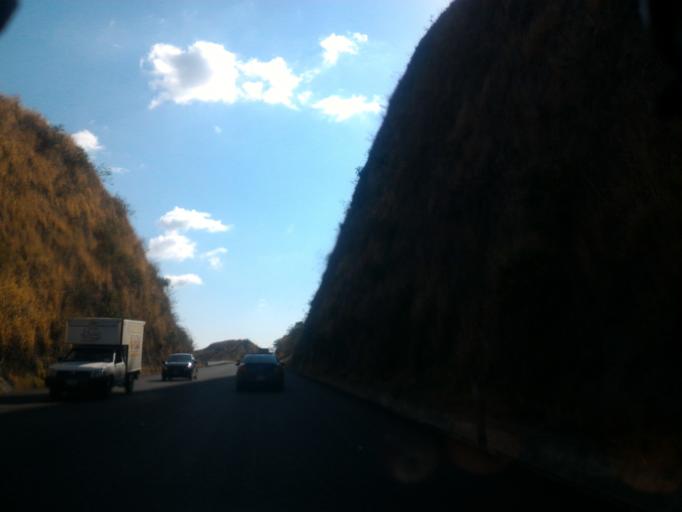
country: MX
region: Jalisco
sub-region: Tonila
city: San Marcos
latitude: 19.4557
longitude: -103.4675
